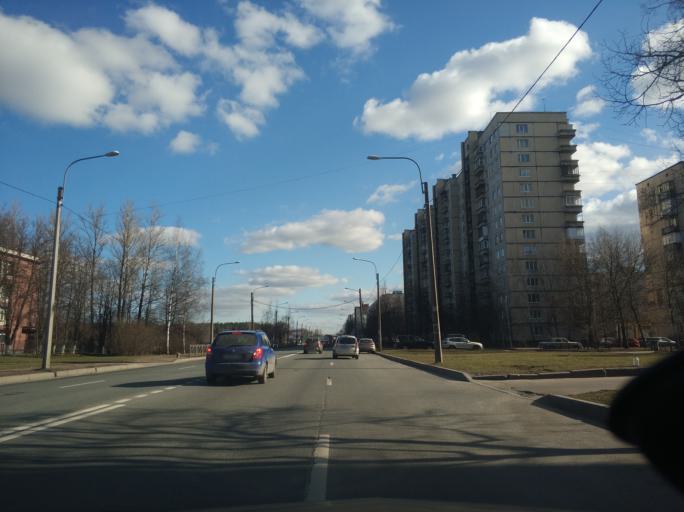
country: RU
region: St.-Petersburg
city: Krasnogvargeisky
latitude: 59.9554
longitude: 30.4953
